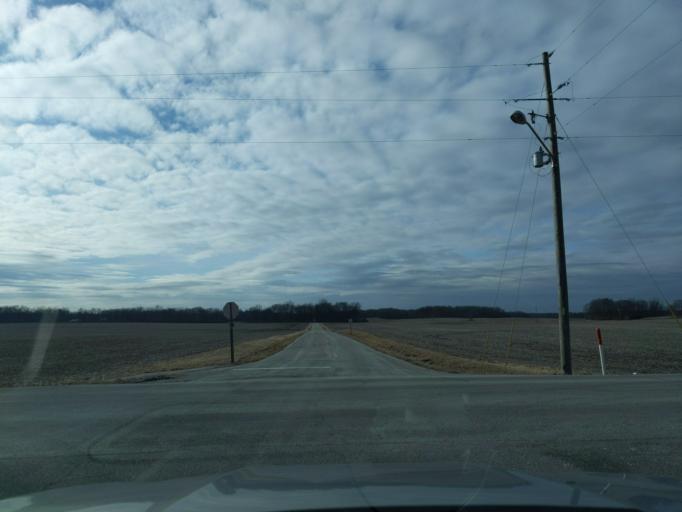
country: US
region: Indiana
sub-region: Tippecanoe County
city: Shadeland
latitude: 40.3376
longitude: -86.9755
